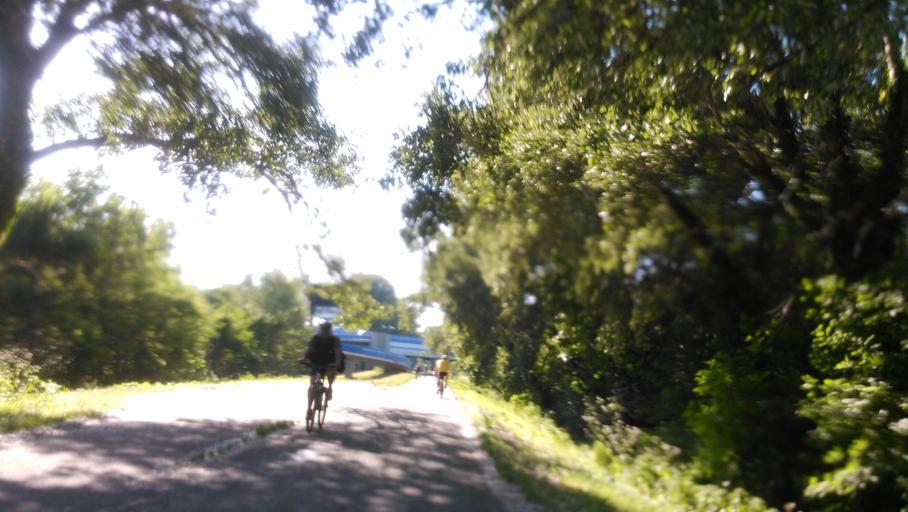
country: SK
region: Bratislavsky
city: Bratislava
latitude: 48.1338
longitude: 17.1303
